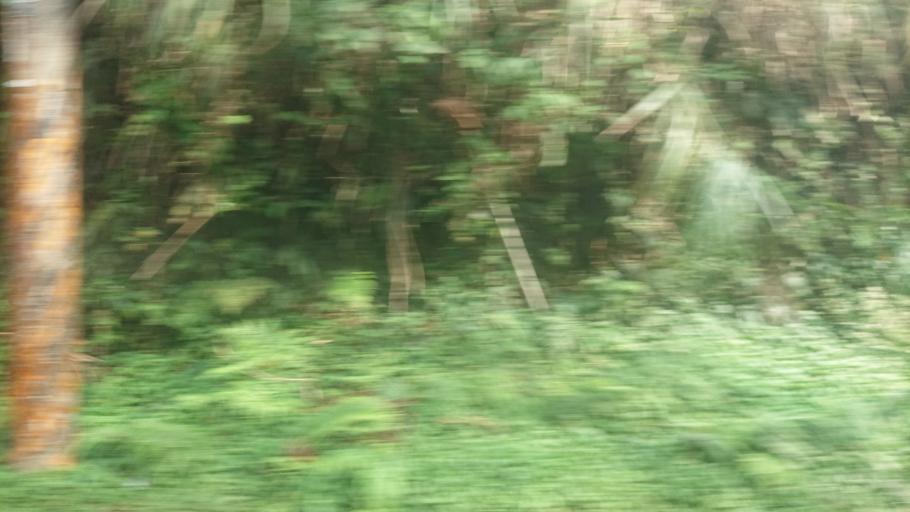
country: TW
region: Taiwan
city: Lugu
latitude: 23.5015
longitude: 120.7829
